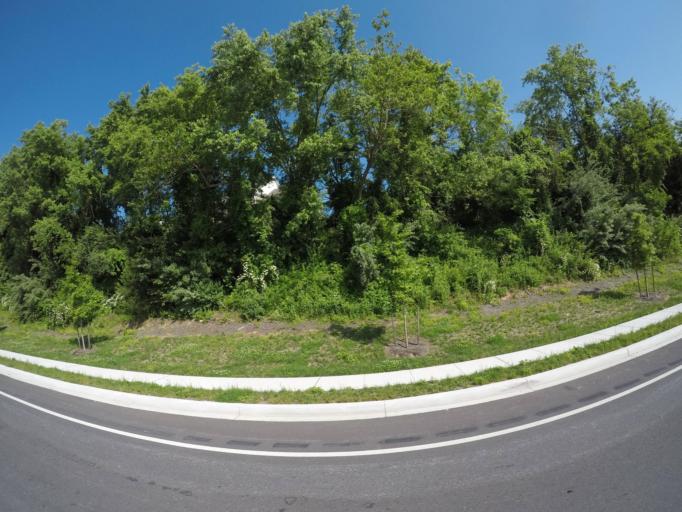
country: US
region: Maryland
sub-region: Howard County
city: Riverside
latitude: 39.1867
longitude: -76.8963
